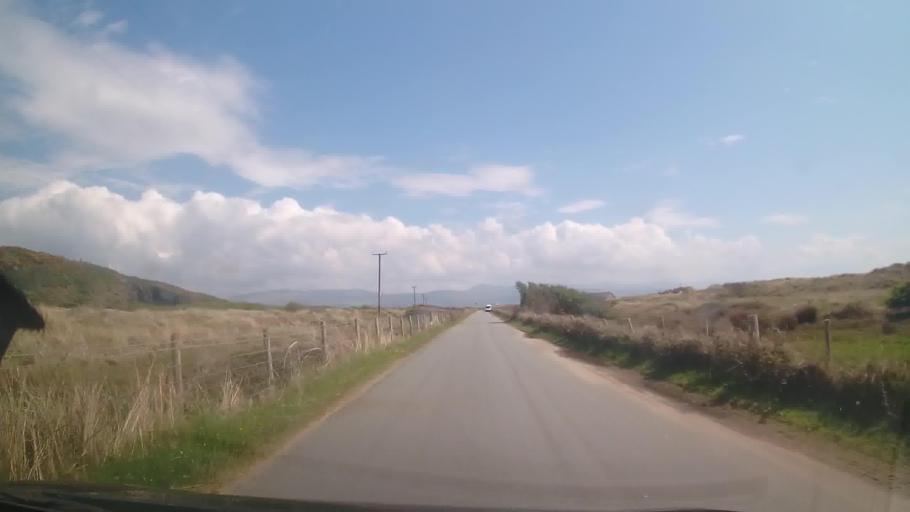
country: GB
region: Wales
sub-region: Gwynedd
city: Criccieth
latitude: 52.9143
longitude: -4.1905
